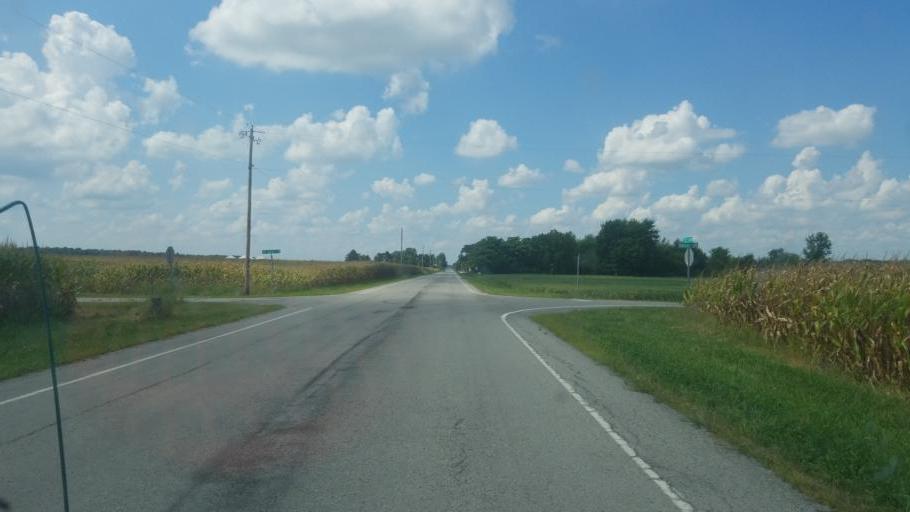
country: US
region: Ohio
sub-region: Hancock County
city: Arlington
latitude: 40.8339
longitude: -83.7273
